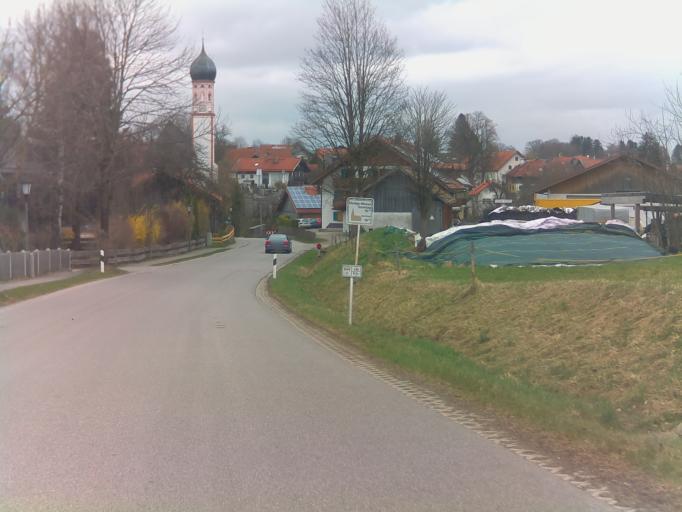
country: DE
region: Bavaria
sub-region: Upper Bavaria
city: Uffing
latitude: 47.7143
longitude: 11.1456
